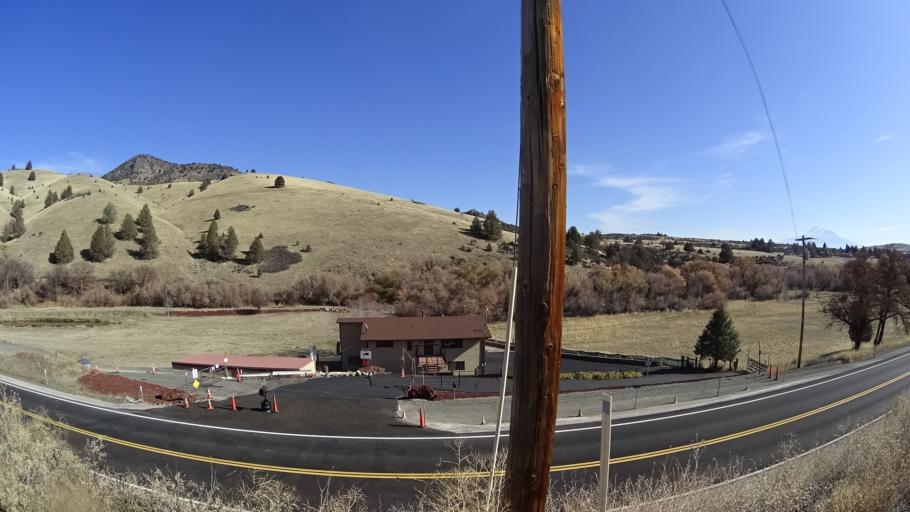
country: US
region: California
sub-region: Siskiyou County
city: Yreka
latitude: 41.7797
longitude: -122.5963
